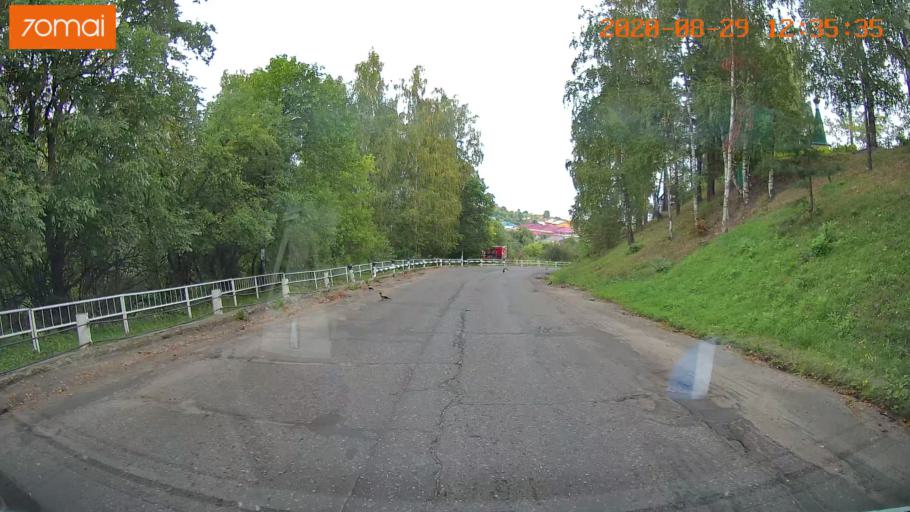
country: RU
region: Ivanovo
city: Yur'yevets
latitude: 57.3139
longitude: 43.1074
